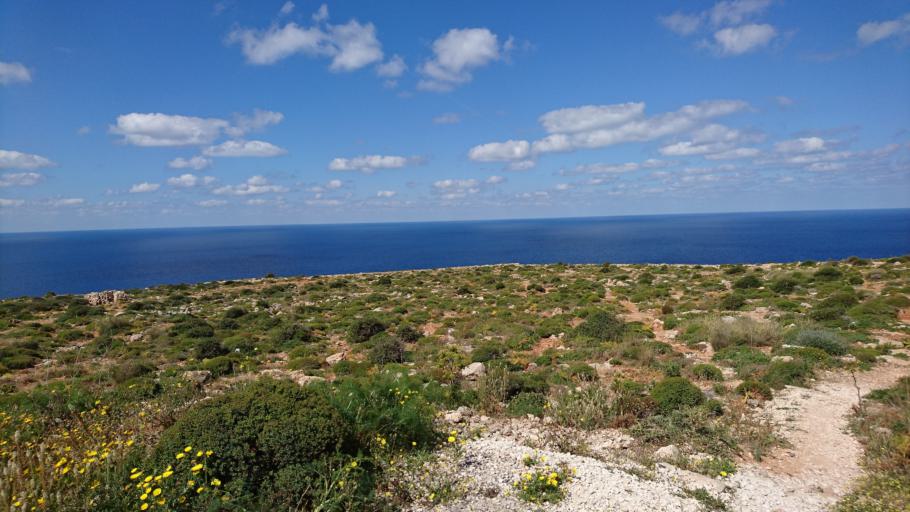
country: MT
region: Il-Mellieha
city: Mellieha
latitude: 35.9718
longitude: 14.3243
